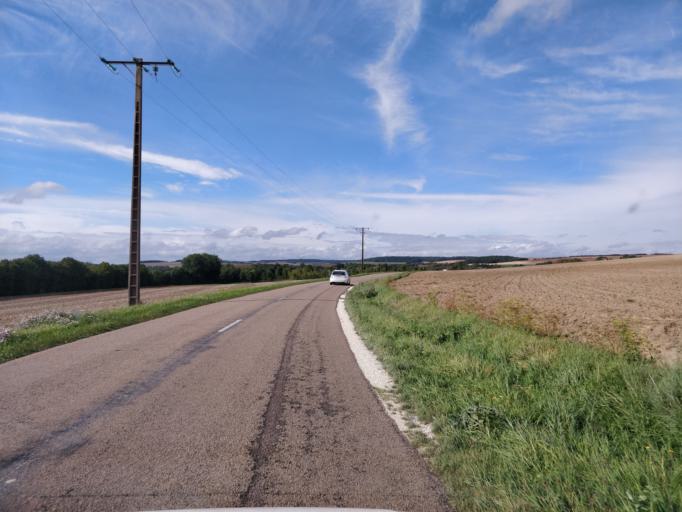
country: FR
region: Champagne-Ardenne
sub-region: Departement de l'Aube
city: Aix-en-Othe
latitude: 48.2198
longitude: 3.6198
